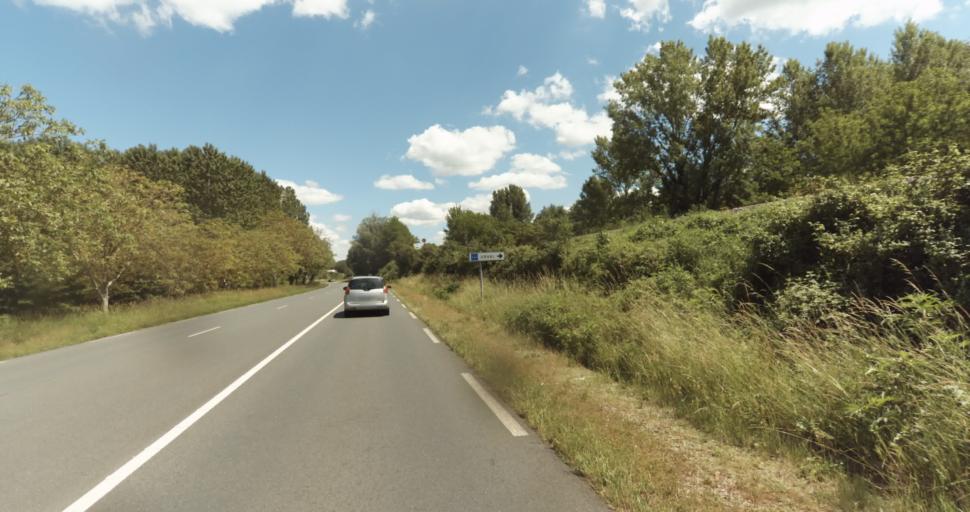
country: FR
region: Aquitaine
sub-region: Departement de la Dordogne
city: Belves
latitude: 44.8220
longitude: 0.9636
